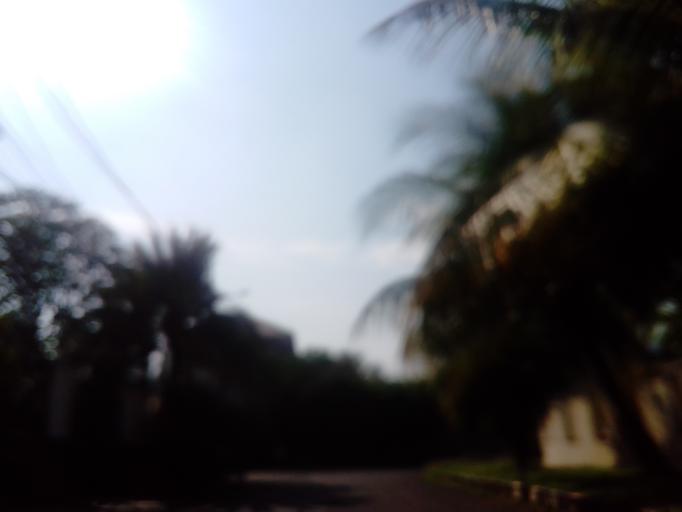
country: ID
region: Jakarta Raya
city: Jakarta
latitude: -6.2554
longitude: 106.8035
